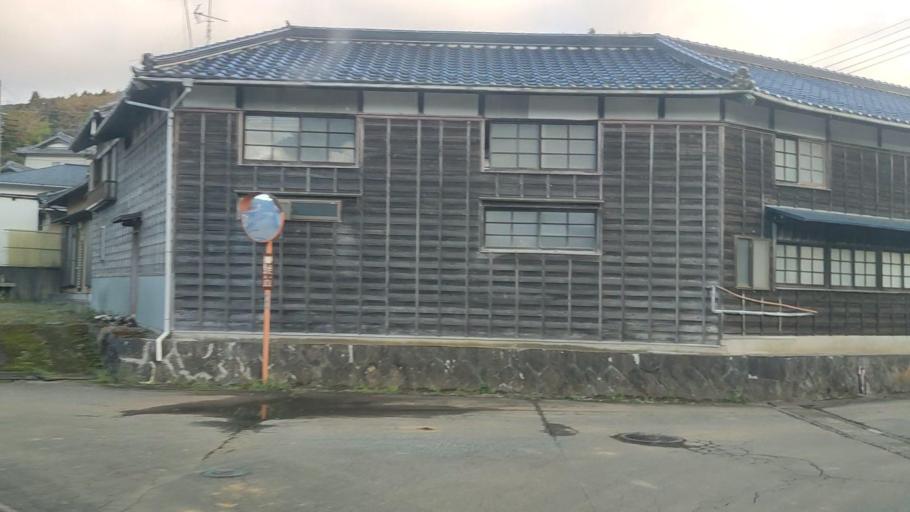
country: JP
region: Kanagawa
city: Yugawara
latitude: 35.1272
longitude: 139.0155
